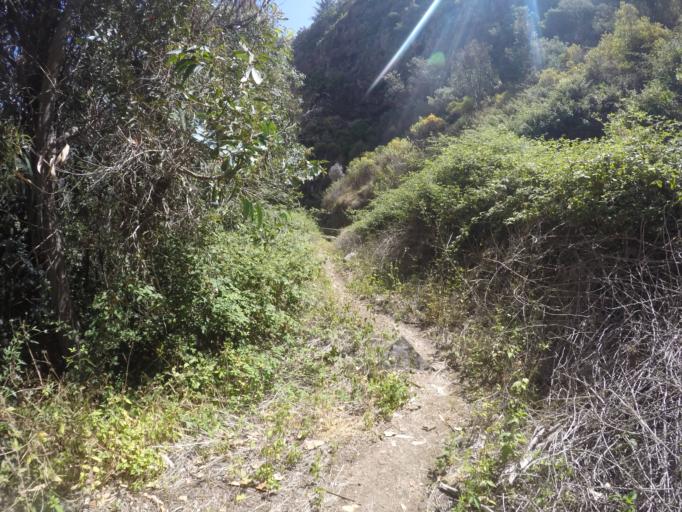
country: PT
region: Madeira
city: Camara de Lobos
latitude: 32.6680
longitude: -16.9589
